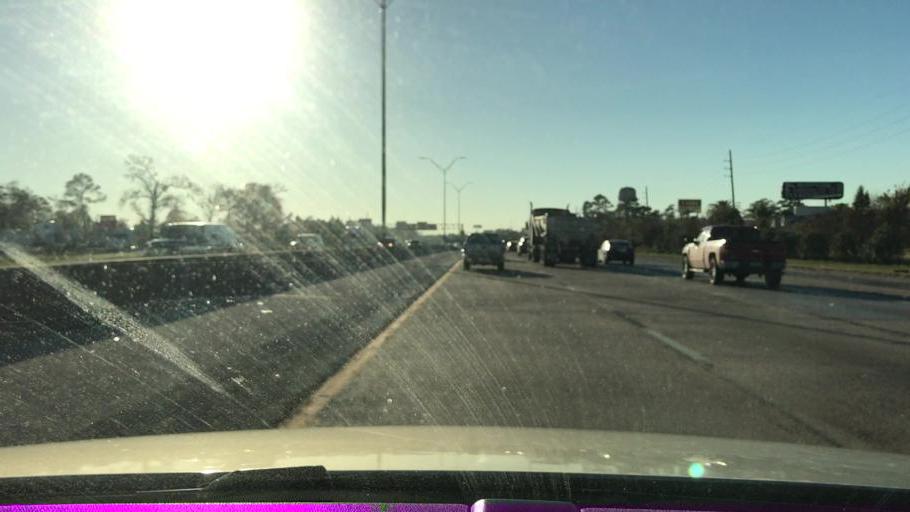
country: US
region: Texas
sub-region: Harris County
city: Channelview
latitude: 29.7873
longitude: -95.0999
